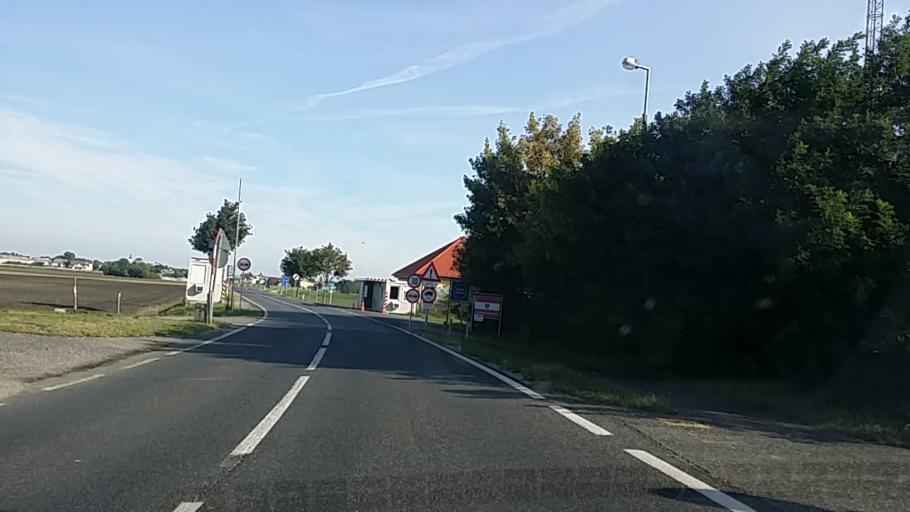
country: AT
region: Burgenland
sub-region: Politischer Bezirk Neusiedl am See
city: Pamhagen
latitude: 47.6875
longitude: 16.9127
